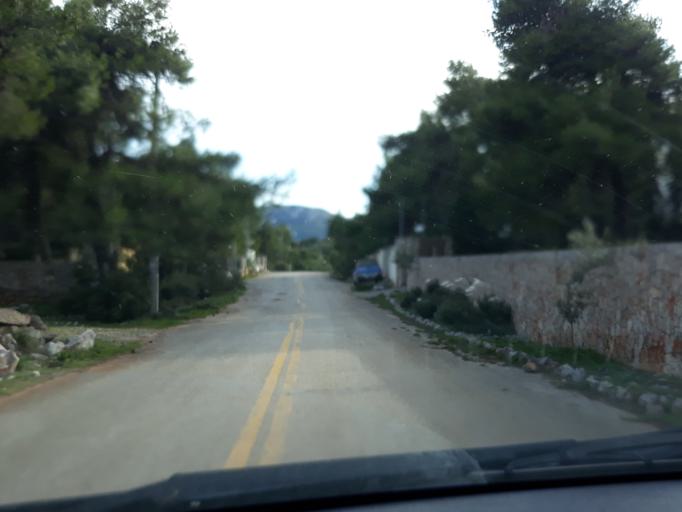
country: GR
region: Attica
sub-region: Nomarchia Anatolikis Attikis
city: Afidnes
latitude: 38.2151
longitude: 23.7977
